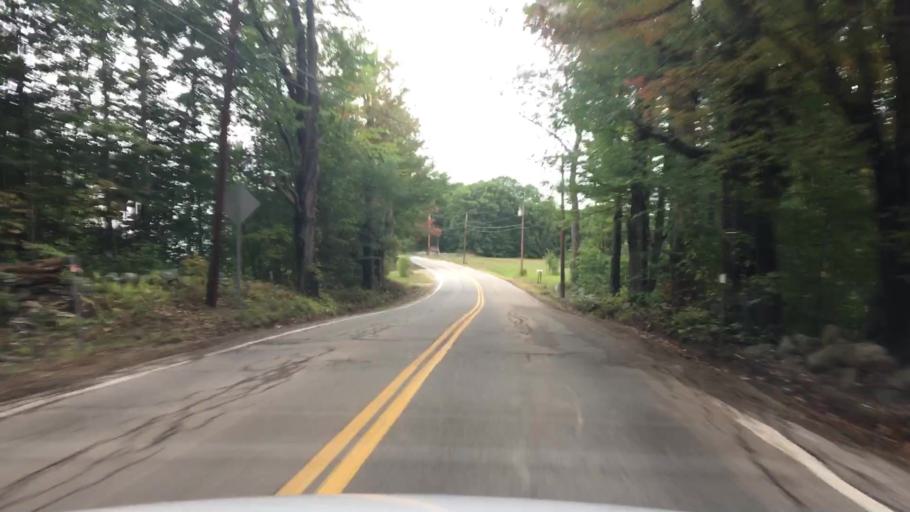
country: US
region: New Hampshire
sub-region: Carroll County
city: Effingham
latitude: 43.7672
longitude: -70.9974
